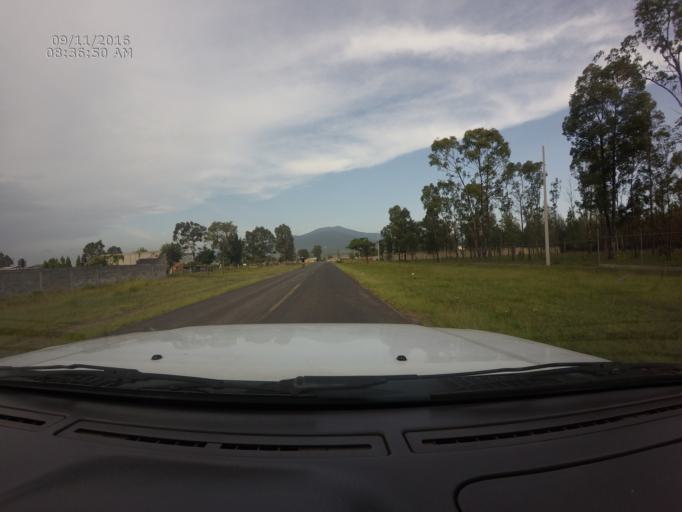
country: MX
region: Michoacan
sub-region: Morelia
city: La Mintzita (Piedra Dura)
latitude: 19.6226
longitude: -101.2697
